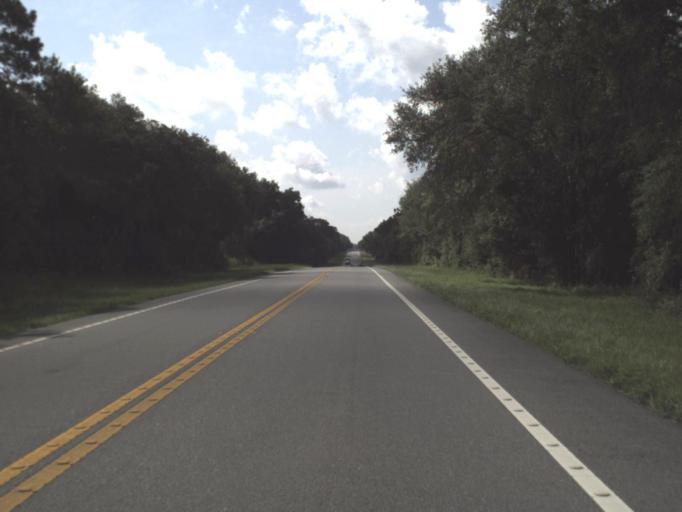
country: US
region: Florida
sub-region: Citrus County
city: Citrus Springs
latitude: 28.9898
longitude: -82.4382
